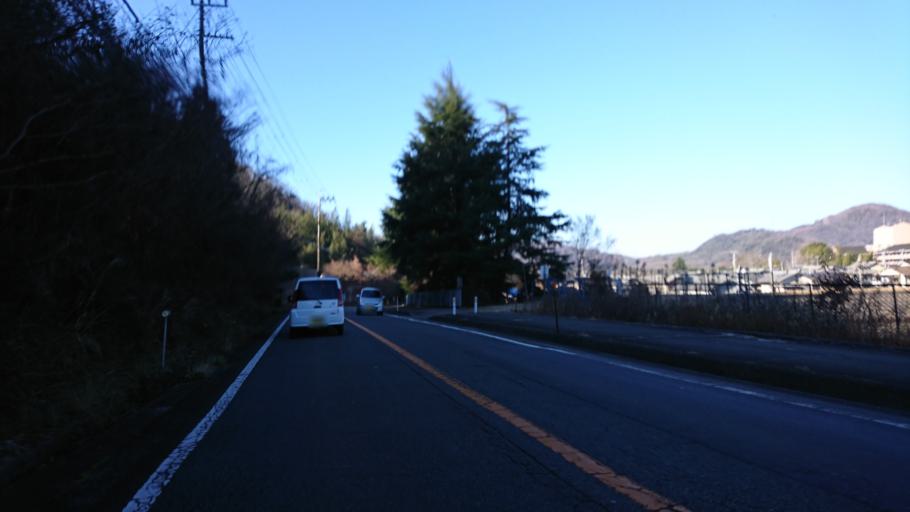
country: JP
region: Hyogo
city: Kakogawacho-honmachi
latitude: 34.8389
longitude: 134.8446
